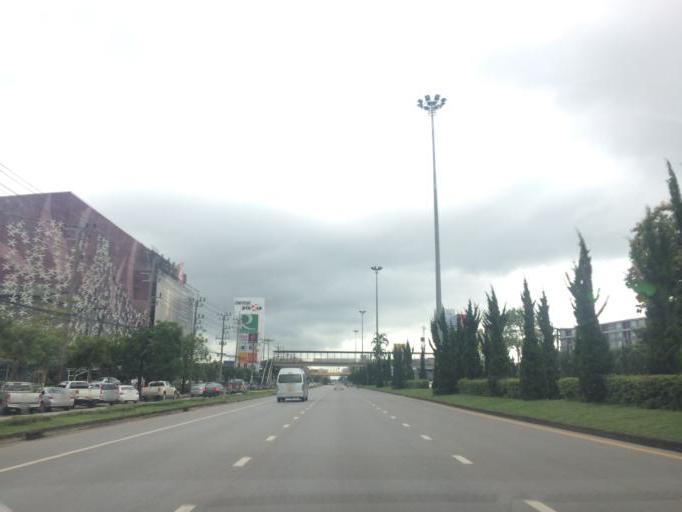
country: TH
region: Chiang Rai
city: Chiang Rai
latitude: 19.8852
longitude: 99.8350
